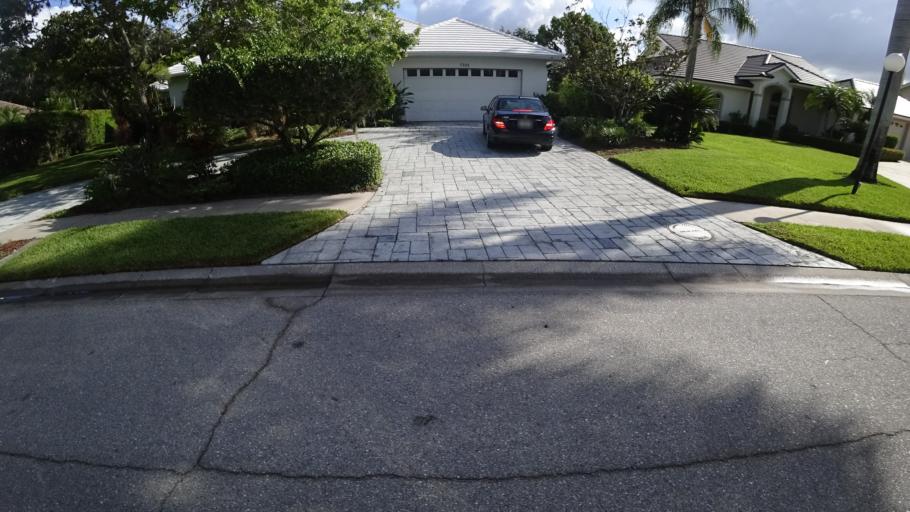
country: US
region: Florida
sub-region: Sarasota County
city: Desoto Lakes
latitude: 27.4095
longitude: -82.4839
